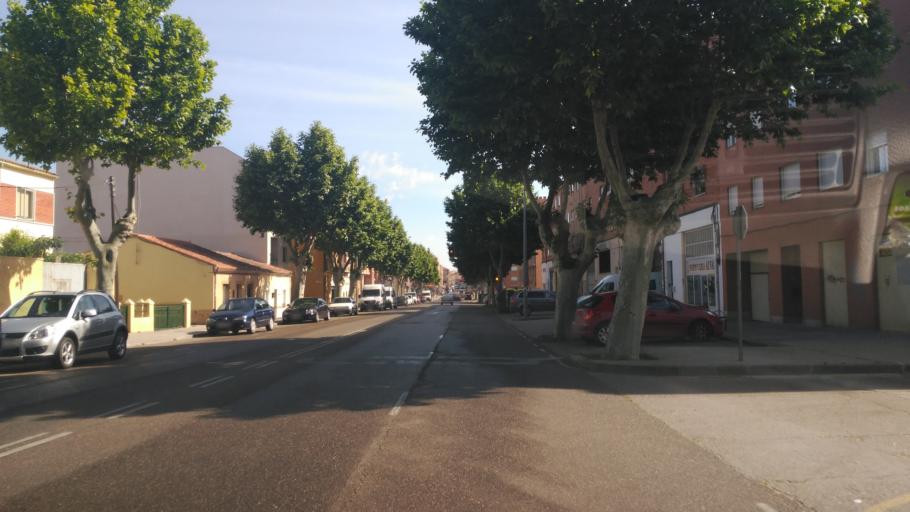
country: ES
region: Castille and Leon
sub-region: Provincia de Zamora
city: Zamora
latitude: 41.4927
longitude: -5.7426
